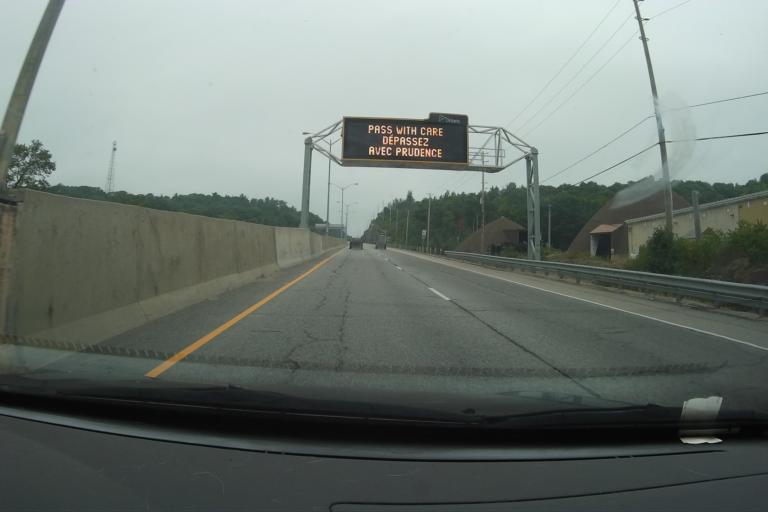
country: CA
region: Ontario
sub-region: Nipissing District
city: North Bay
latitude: 46.3380
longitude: -79.4677
